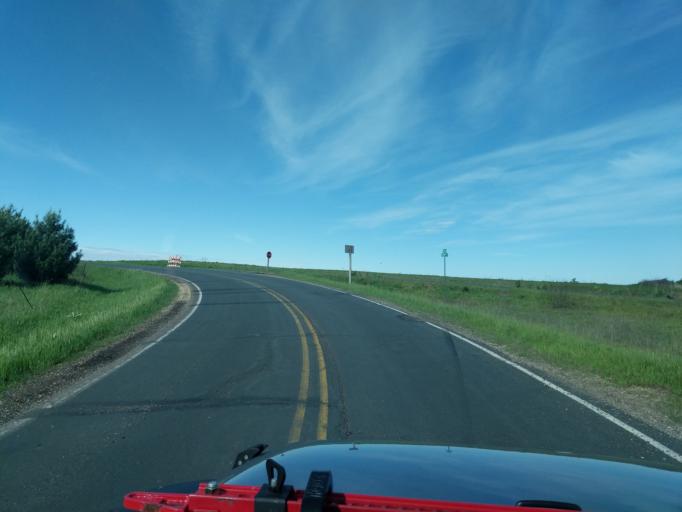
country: US
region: Wisconsin
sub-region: Saint Croix County
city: Hammond
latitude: 44.8806
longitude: -92.4963
